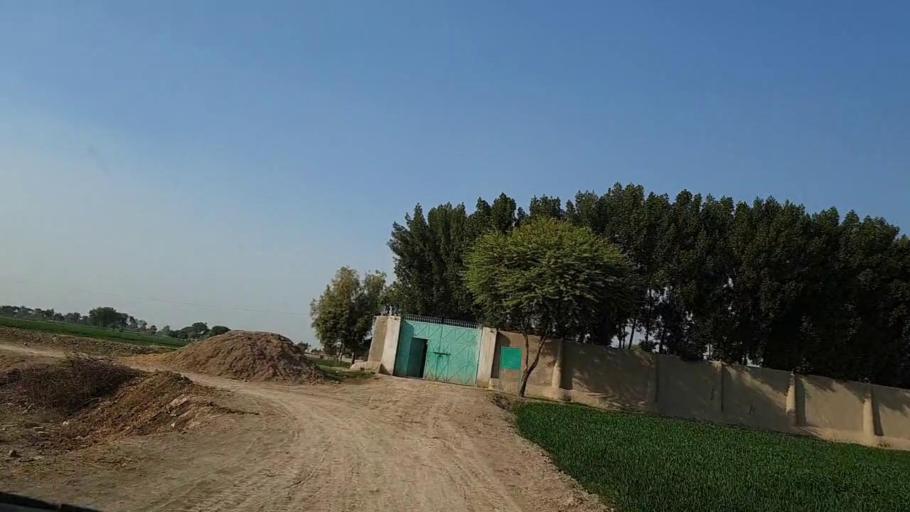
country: PK
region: Sindh
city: Sakrand
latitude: 26.1218
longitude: 68.2402
